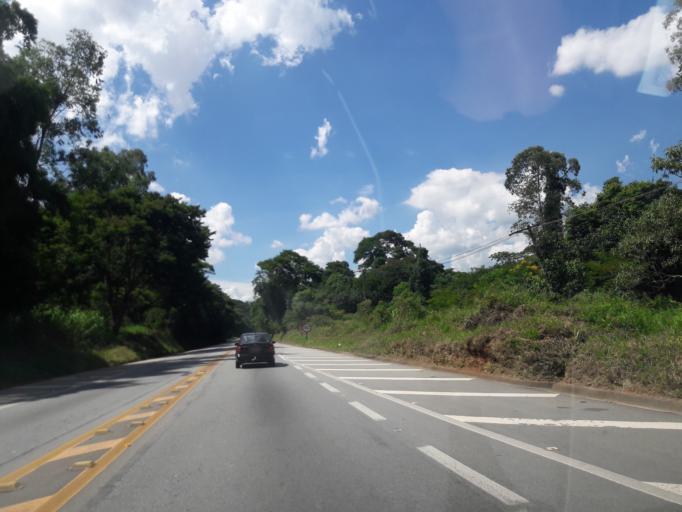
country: BR
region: Sao Paulo
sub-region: Francisco Morato
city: Francisco Morato
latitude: -23.3013
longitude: -46.8099
